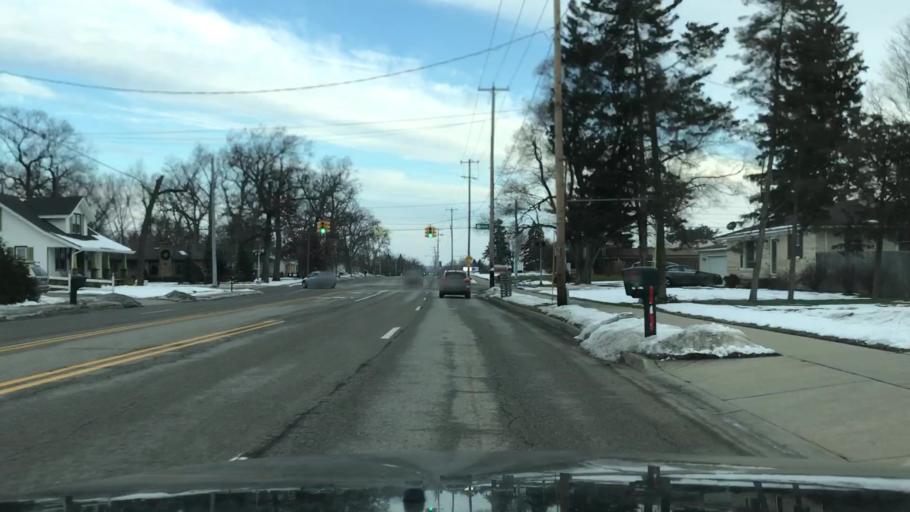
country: US
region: Michigan
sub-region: Kent County
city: Grandville
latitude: 42.9056
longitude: -85.7439
